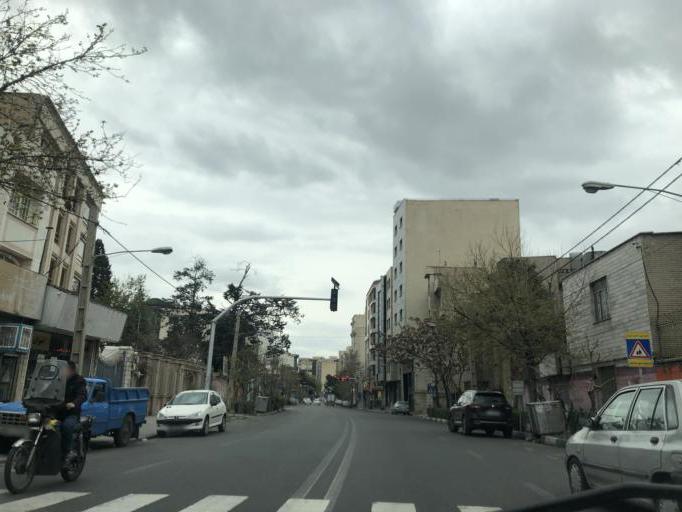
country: IR
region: Tehran
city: Tajrish
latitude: 35.7800
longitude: 51.4560
